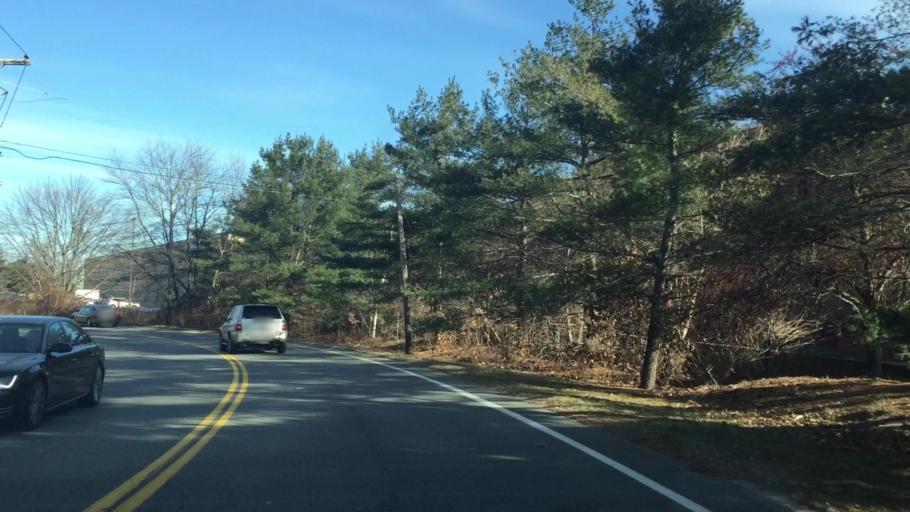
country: US
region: New Hampshire
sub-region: Rockingham County
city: Salem
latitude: 42.7680
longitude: -71.2328
